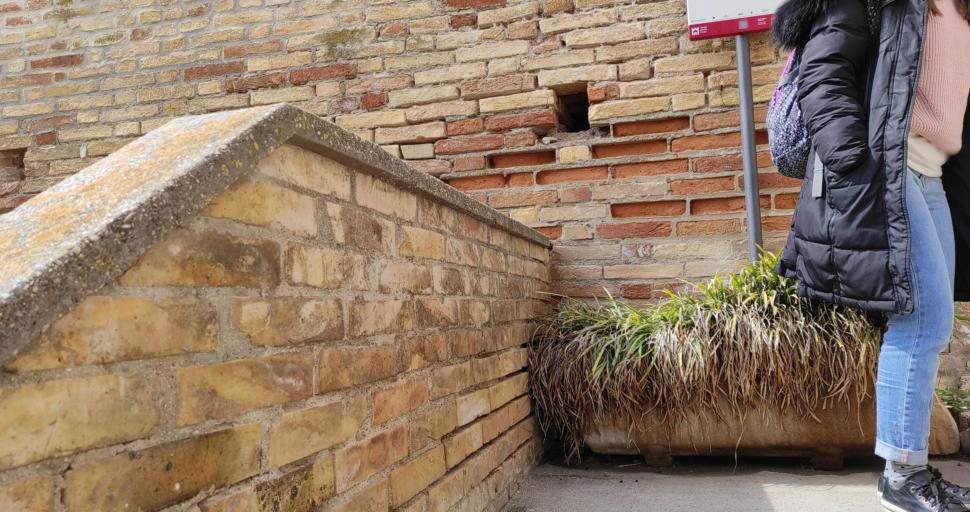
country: IT
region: The Marches
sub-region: Province of Fermo
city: Altidona
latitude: 43.1414
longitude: 13.8115
